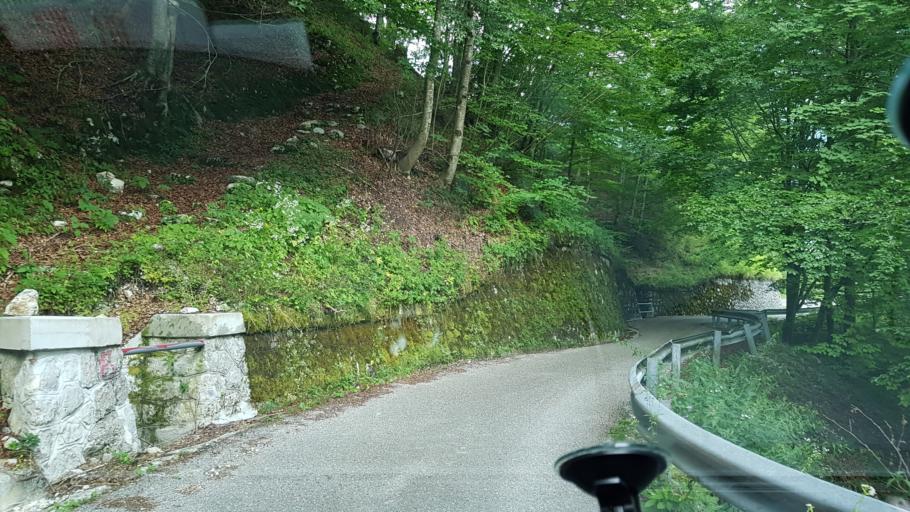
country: IT
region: Friuli Venezia Giulia
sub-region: Provincia di Udine
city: Taipana
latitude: 46.3152
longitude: 13.3922
